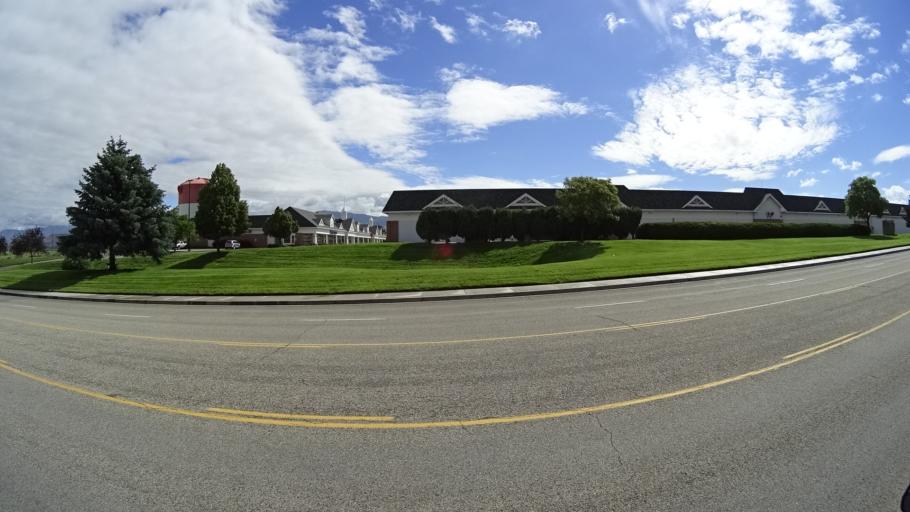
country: US
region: Idaho
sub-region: Ada County
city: Boise
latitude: 43.5393
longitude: -116.1638
